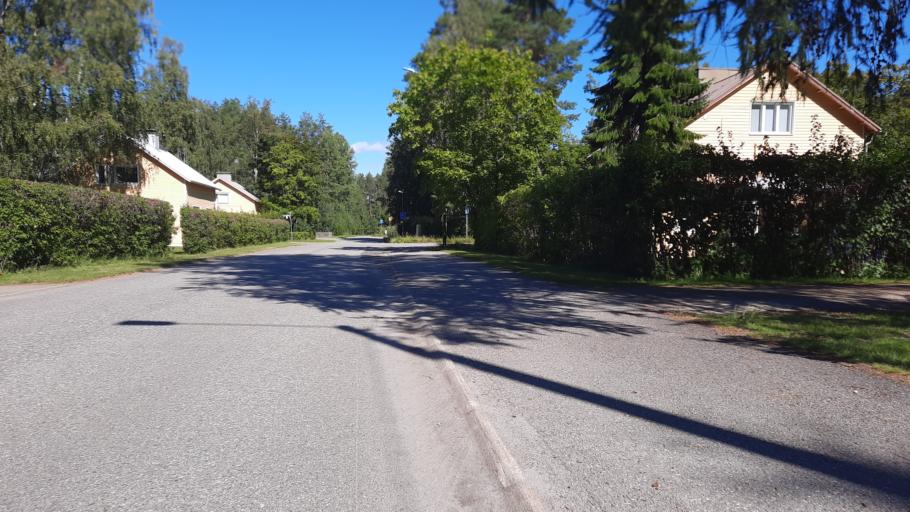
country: FI
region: North Karelia
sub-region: Joensuu
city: Joensuu
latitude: 62.6219
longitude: 29.7329
